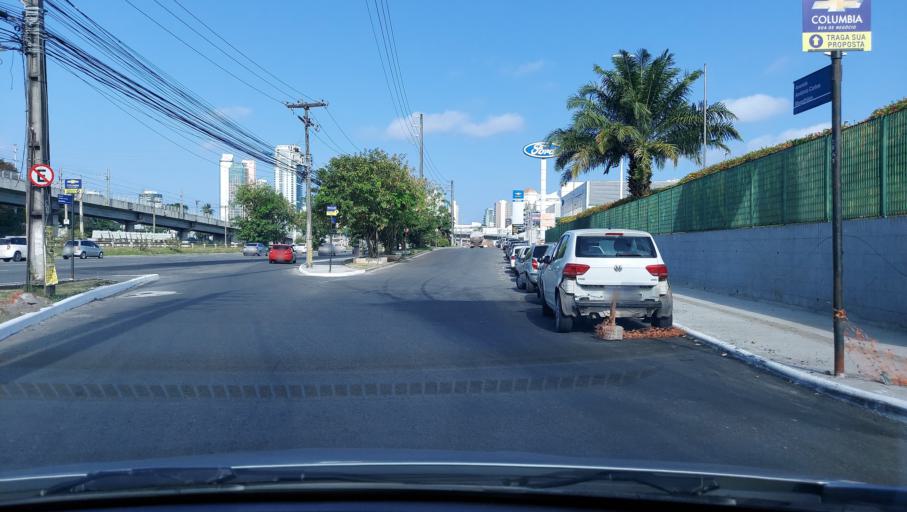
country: BR
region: Bahia
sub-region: Salvador
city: Salvador
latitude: -12.9791
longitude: -38.4703
